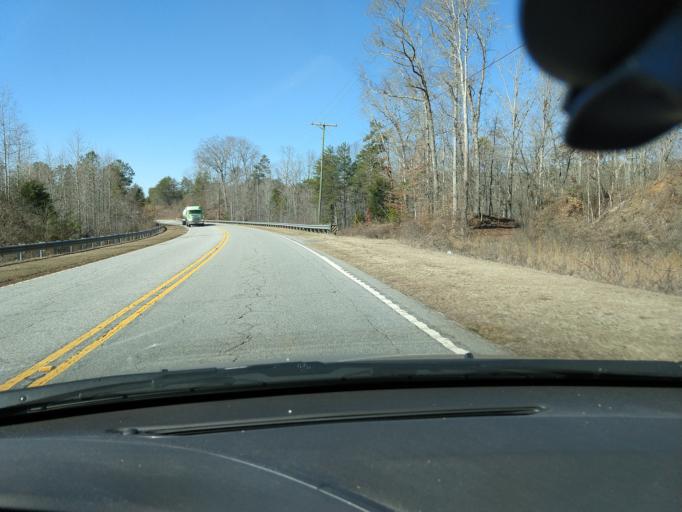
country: US
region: South Carolina
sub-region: Oconee County
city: Westminster
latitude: 34.6102
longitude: -83.1511
